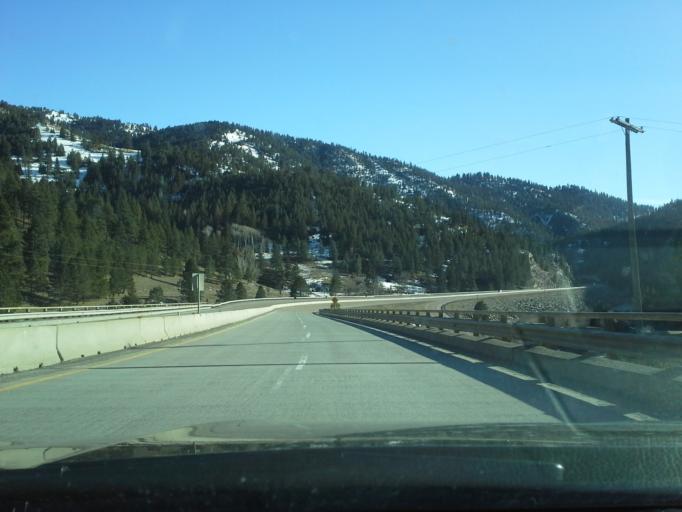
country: US
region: Montana
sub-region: Lewis and Clark County
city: Helena Valley Northwest
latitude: 46.9217
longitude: -112.1230
